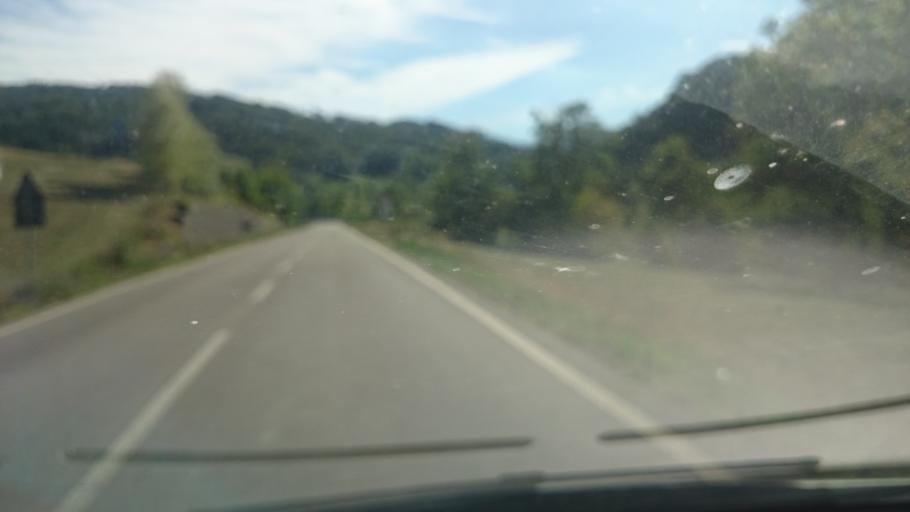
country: IT
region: Emilia-Romagna
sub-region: Provincia di Reggio Emilia
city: Carpineti
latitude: 44.4108
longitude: 10.5250
